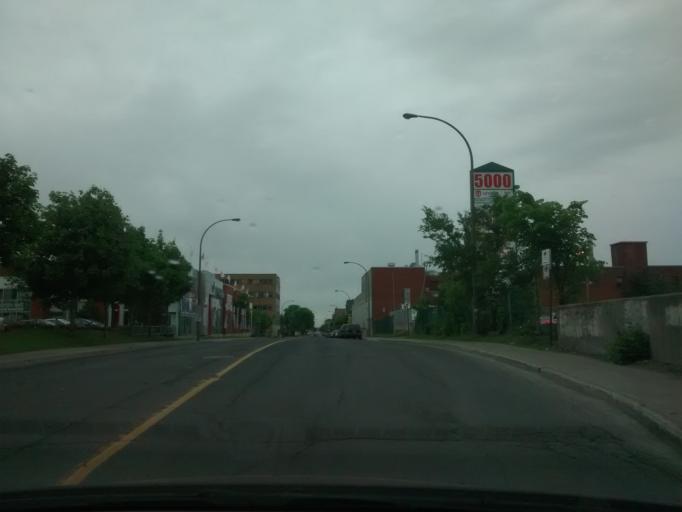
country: CA
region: Quebec
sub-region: Montreal
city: Montreal
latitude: 45.5407
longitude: -73.5726
